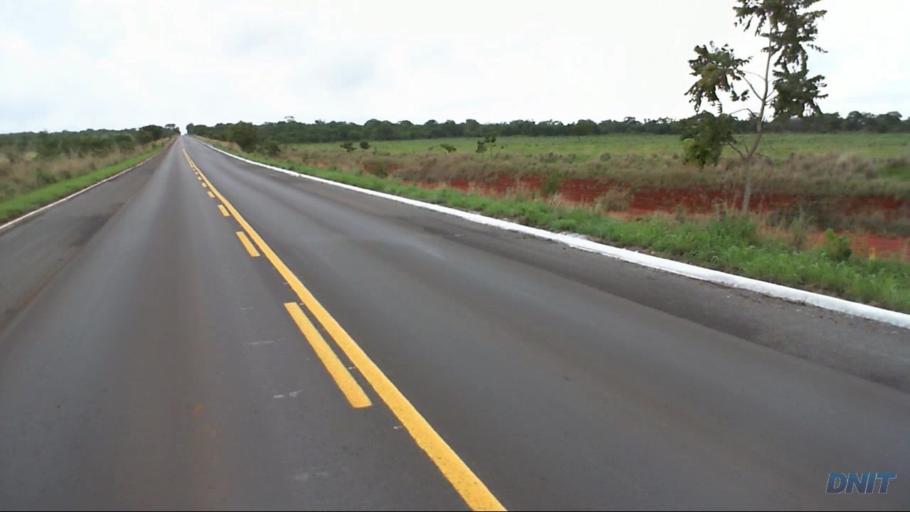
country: BR
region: Goias
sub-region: Padre Bernardo
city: Padre Bernardo
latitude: -15.1760
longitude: -48.4063
